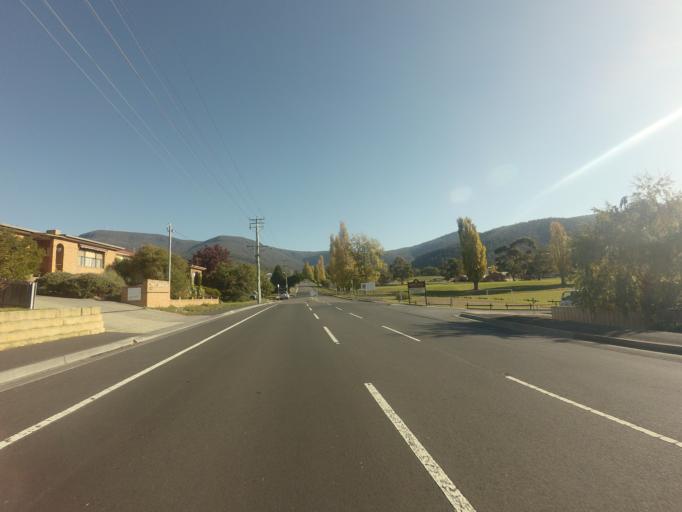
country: AU
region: Tasmania
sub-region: Glenorchy
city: West Moonah
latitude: -42.8484
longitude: 147.2606
